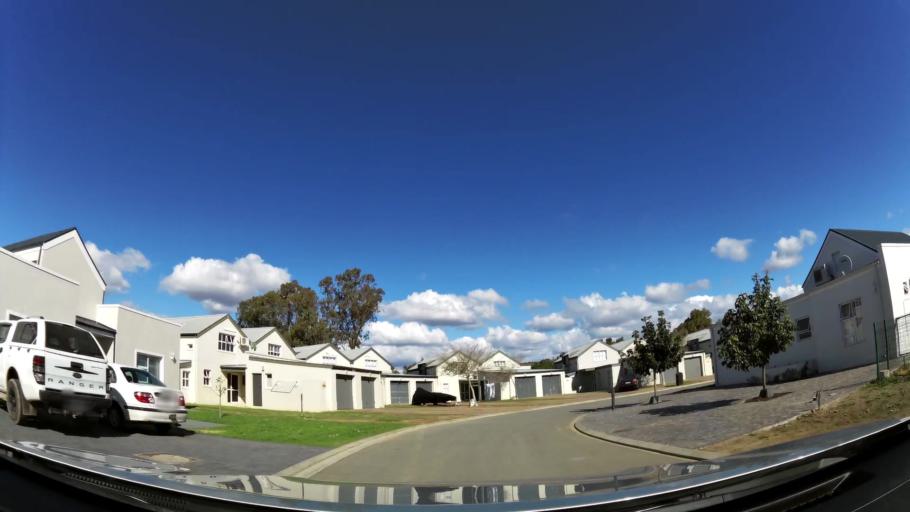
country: ZA
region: Western Cape
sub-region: Cape Winelands District Municipality
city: Ashton
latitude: -33.8119
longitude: 19.8573
